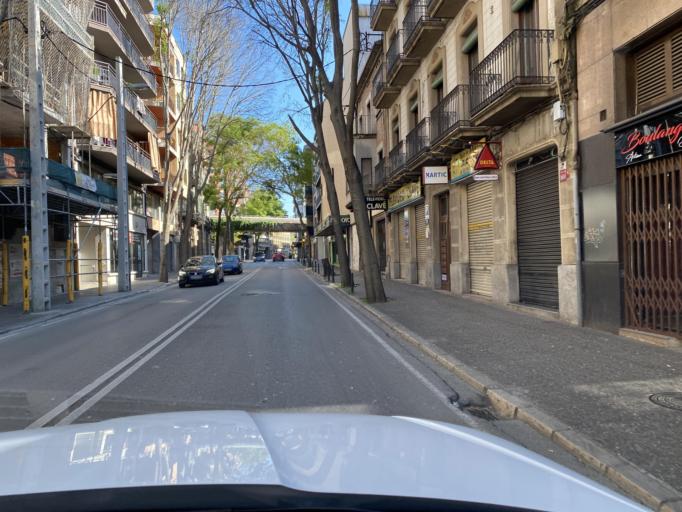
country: ES
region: Catalonia
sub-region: Provincia de Girona
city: Girona
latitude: 41.9842
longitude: 2.8177
